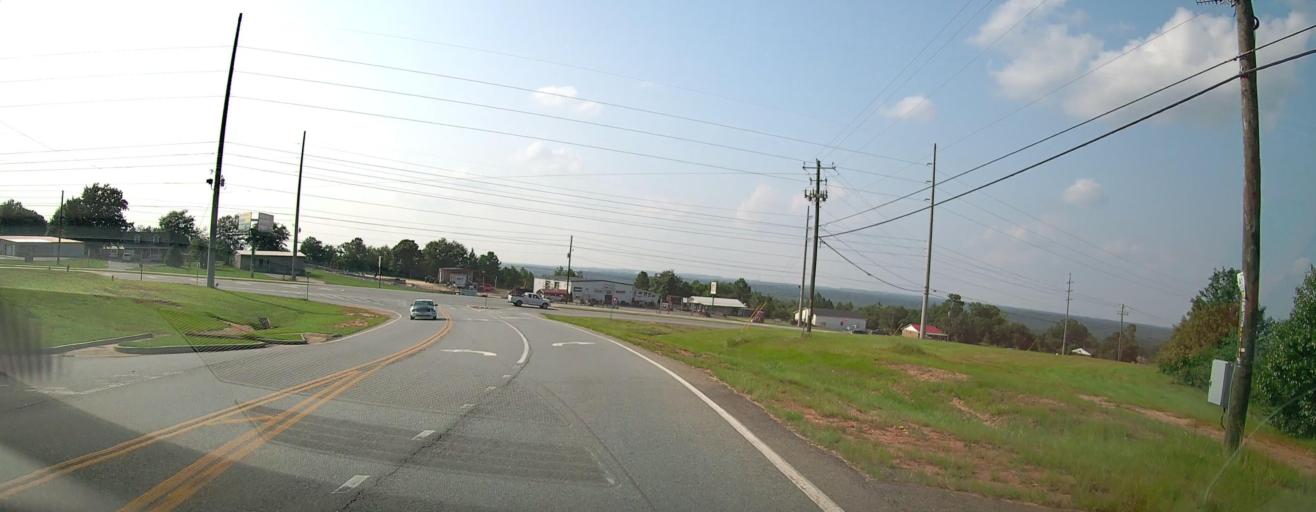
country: US
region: Georgia
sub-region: Houston County
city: Centerville
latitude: 32.6761
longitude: -83.7051
